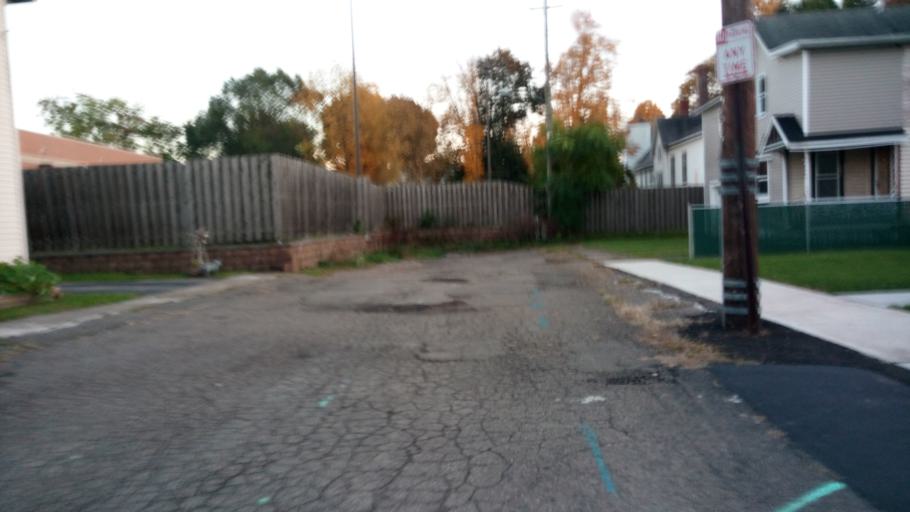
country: US
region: New York
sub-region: Chemung County
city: Elmira
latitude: 42.0784
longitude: -76.8046
